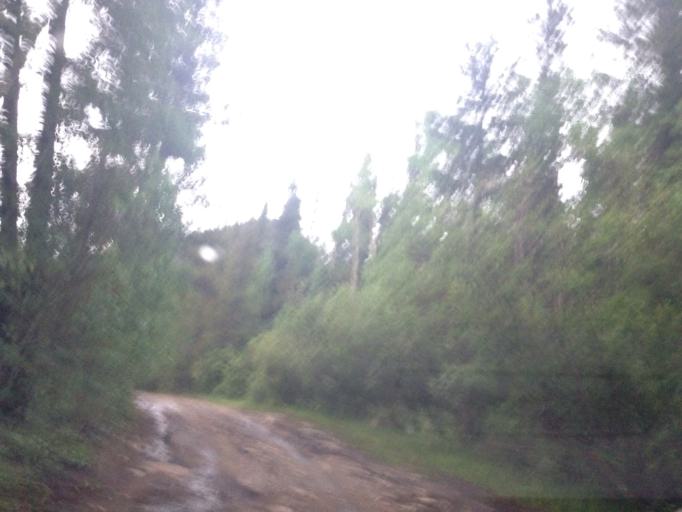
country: US
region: Colorado
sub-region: Clear Creek County
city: Georgetown
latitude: 39.5608
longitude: -105.7635
